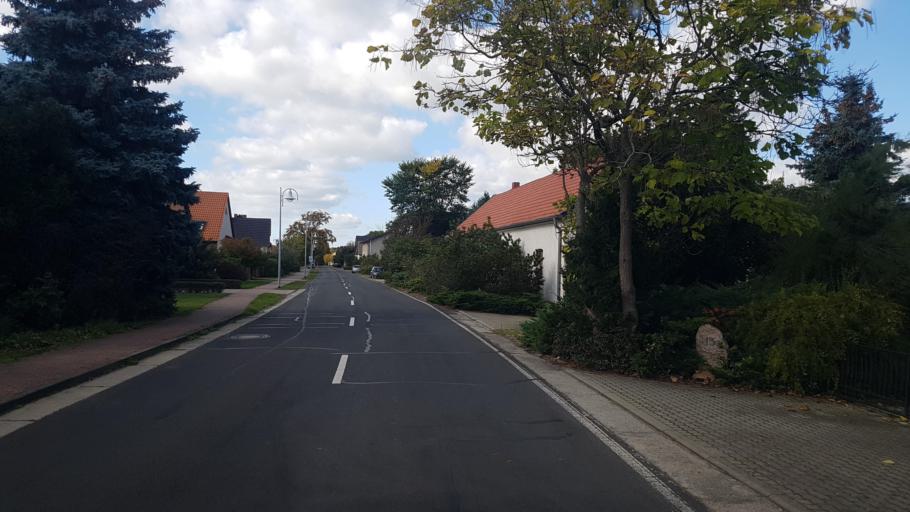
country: DE
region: Brandenburg
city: Peitz
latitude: 51.8094
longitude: 14.4264
